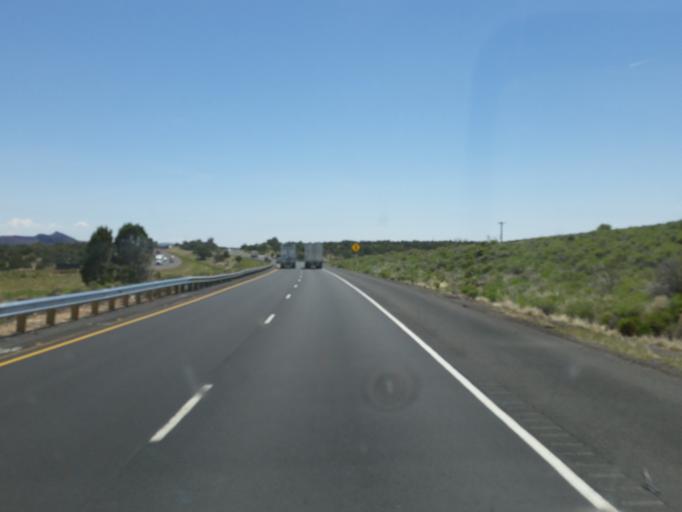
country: US
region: Arizona
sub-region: Coconino County
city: Flagstaff
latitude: 35.2015
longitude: -111.4763
